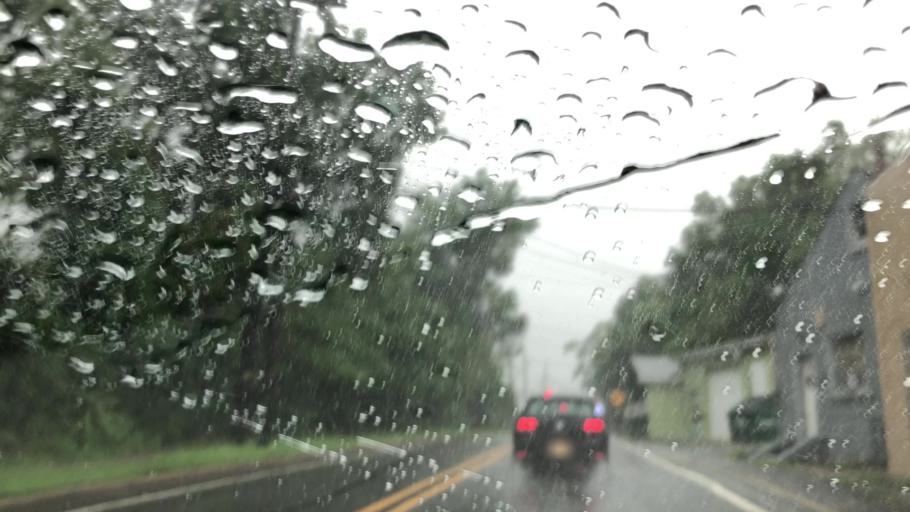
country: US
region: New Jersey
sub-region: Bergen County
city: Saddle Brook
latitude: 40.9015
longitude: -74.1043
